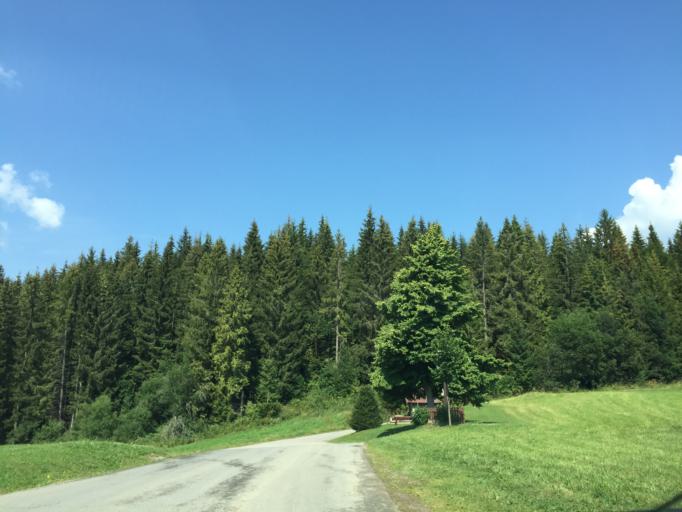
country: SK
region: Zilinsky
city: Oravska Lesna
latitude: 49.4324
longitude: 19.2979
